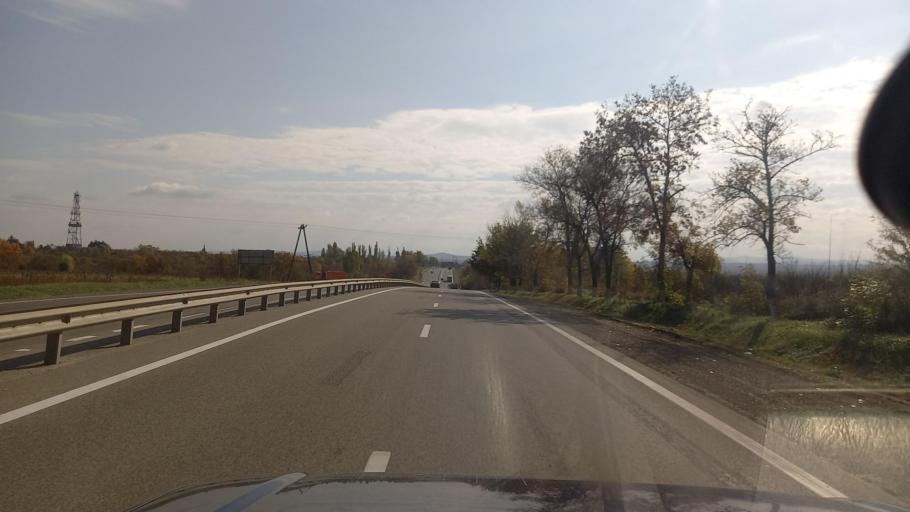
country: RU
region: Krasnodarskiy
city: Akhtyrskiy
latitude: 44.8515
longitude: 38.2697
